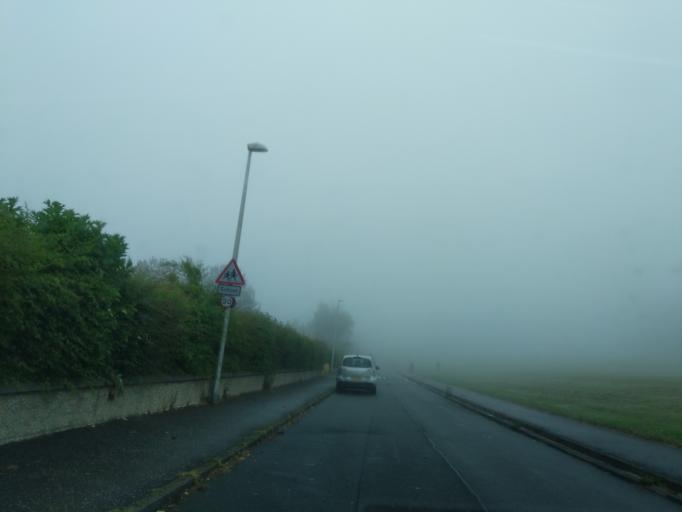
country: GB
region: Scotland
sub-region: West Lothian
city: Seafield
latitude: 55.9485
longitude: -3.1444
